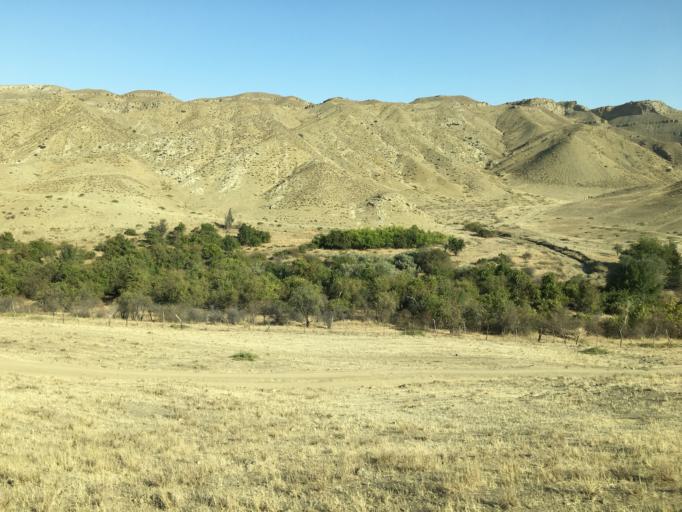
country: TM
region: Balkan
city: Magtymguly
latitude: 38.3020
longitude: 56.7736
